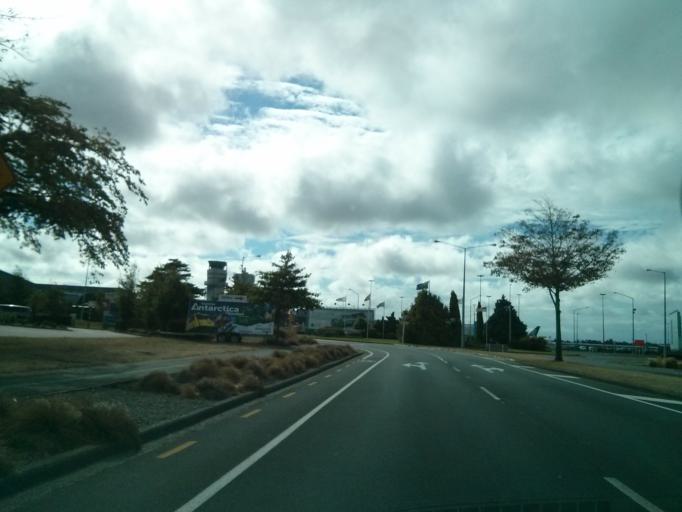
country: NZ
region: Canterbury
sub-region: Selwyn District
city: Prebbleton
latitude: -43.4901
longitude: 172.5454
